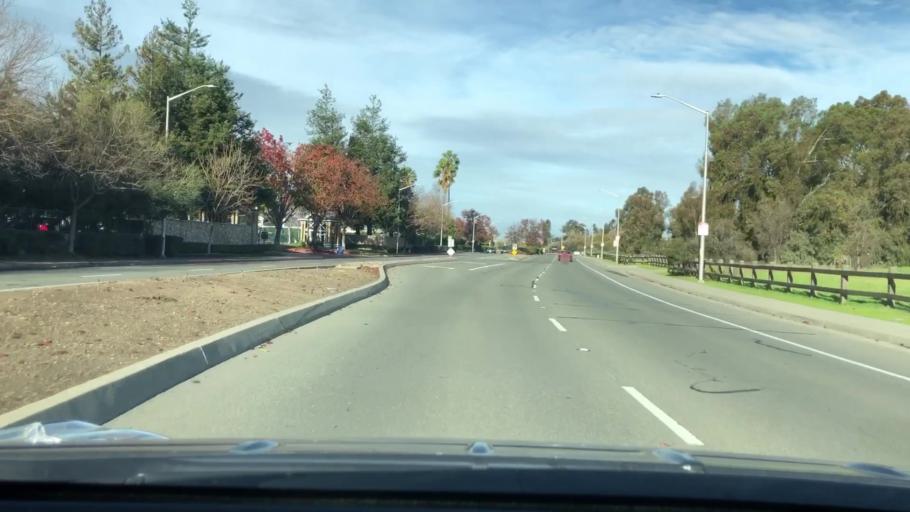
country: US
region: California
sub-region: Santa Clara County
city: Santa Clara
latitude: 37.4048
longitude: -121.9562
